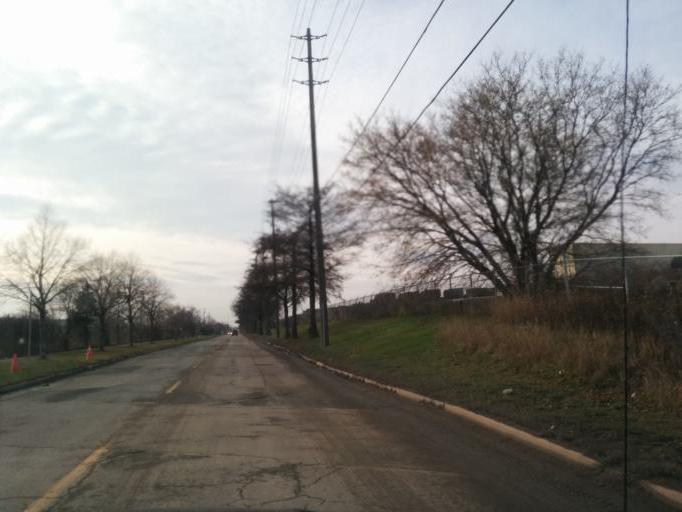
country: CA
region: Ontario
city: Etobicoke
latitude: 43.6061
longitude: -79.5098
